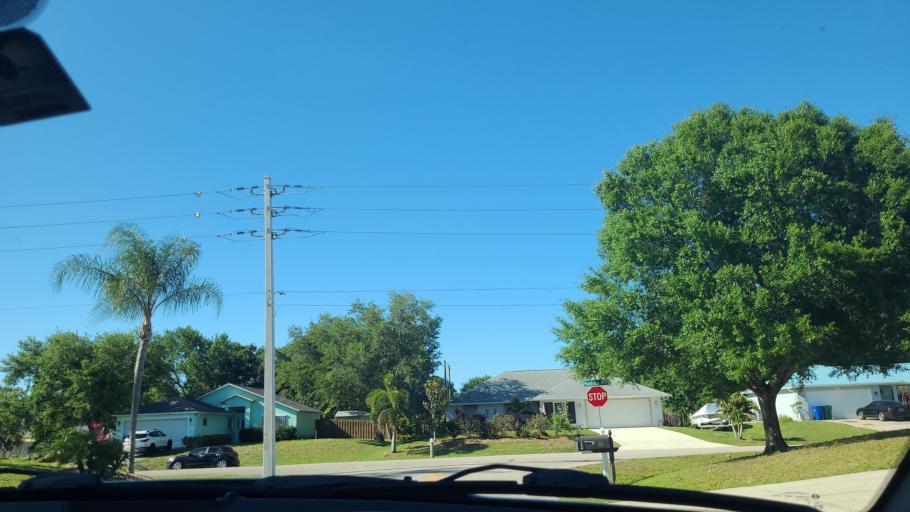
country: US
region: Florida
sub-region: Indian River County
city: Sebastian
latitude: 27.7669
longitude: -80.4966
